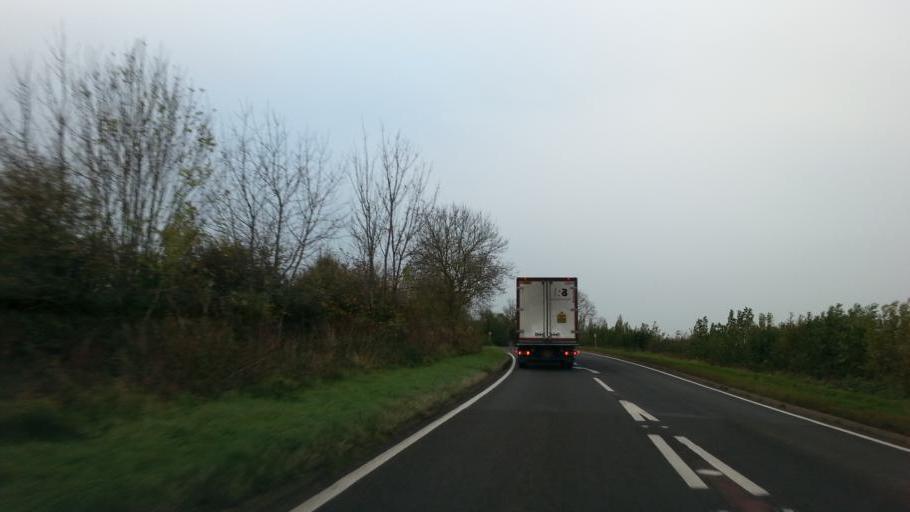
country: GB
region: England
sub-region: District of Rutland
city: Tinwell
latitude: 52.6292
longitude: -0.4972
